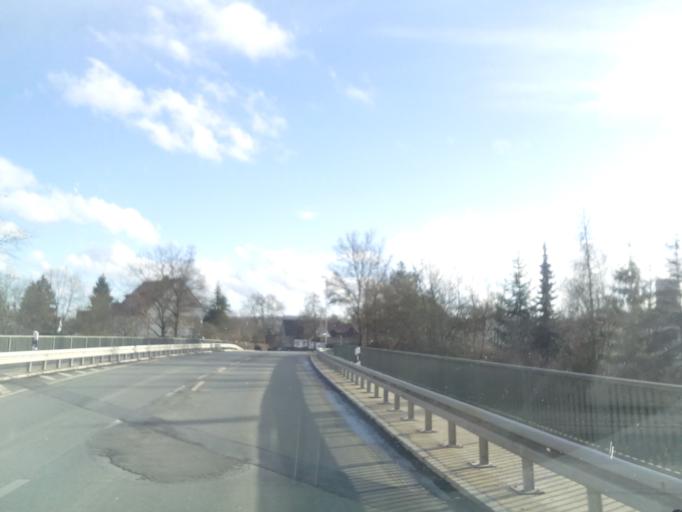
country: DE
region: Bavaria
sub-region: Upper Franconia
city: Mainleus
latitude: 50.1026
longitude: 11.3718
